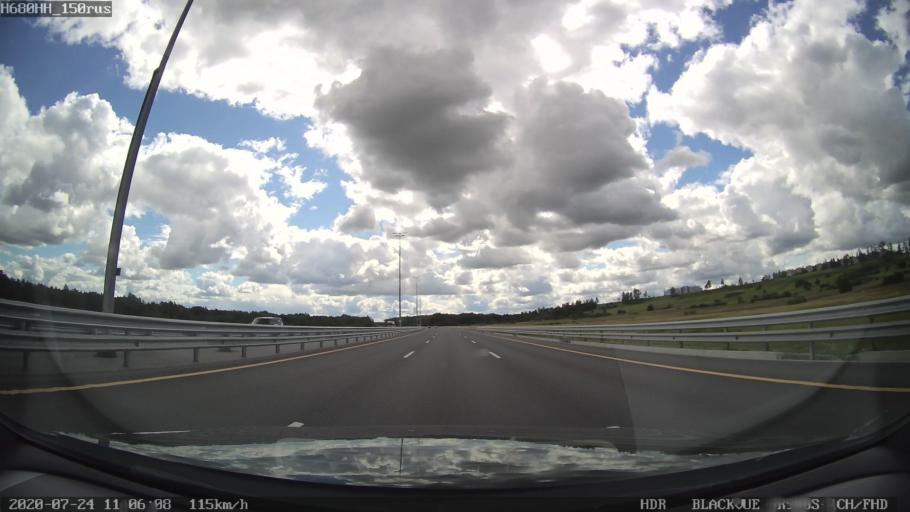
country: RU
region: St.-Petersburg
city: Shushary
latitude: 59.7675
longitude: 30.3678
